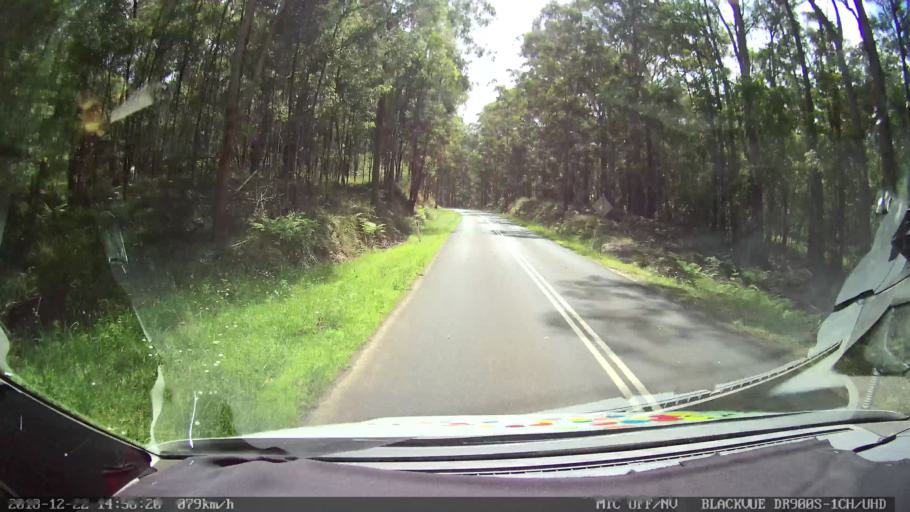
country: AU
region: New South Wales
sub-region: Bellingen
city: Dorrigo
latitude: -30.2325
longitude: 152.5137
